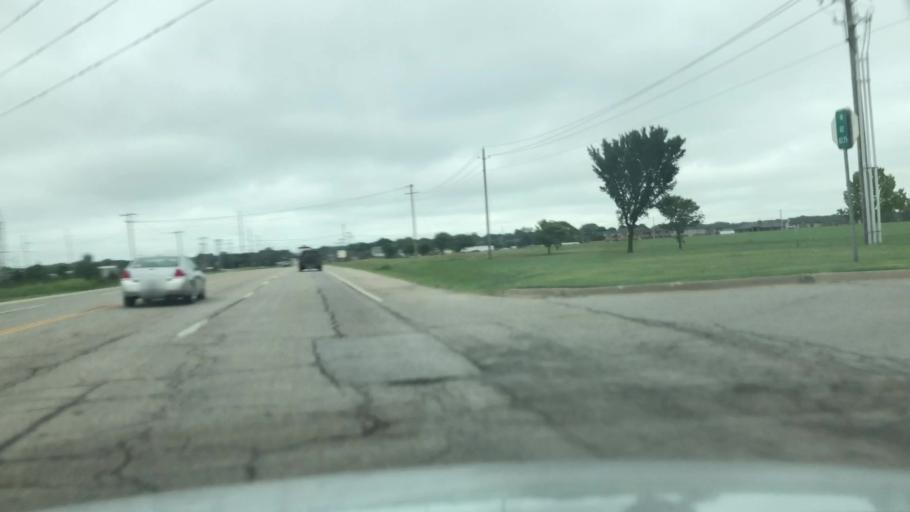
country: US
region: Oklahoma
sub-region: Washington County
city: Dewey
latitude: 36.7280
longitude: -95.8950
